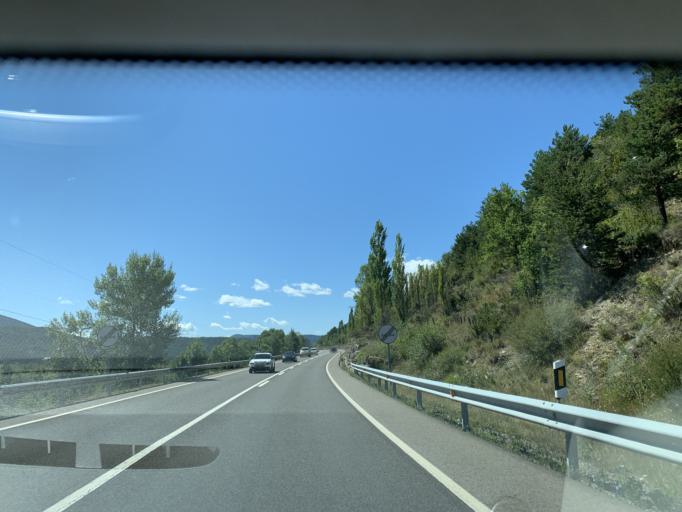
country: ES
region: Aragon
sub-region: Provincia de Huesca
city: Biescas
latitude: 42.5752
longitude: -0.3243
